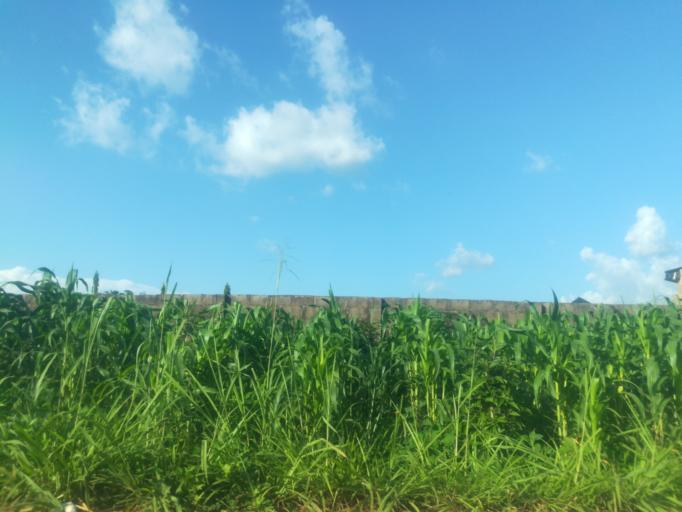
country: NG
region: Oyo
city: Ibadan
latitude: 7.4351
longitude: 3.9737
